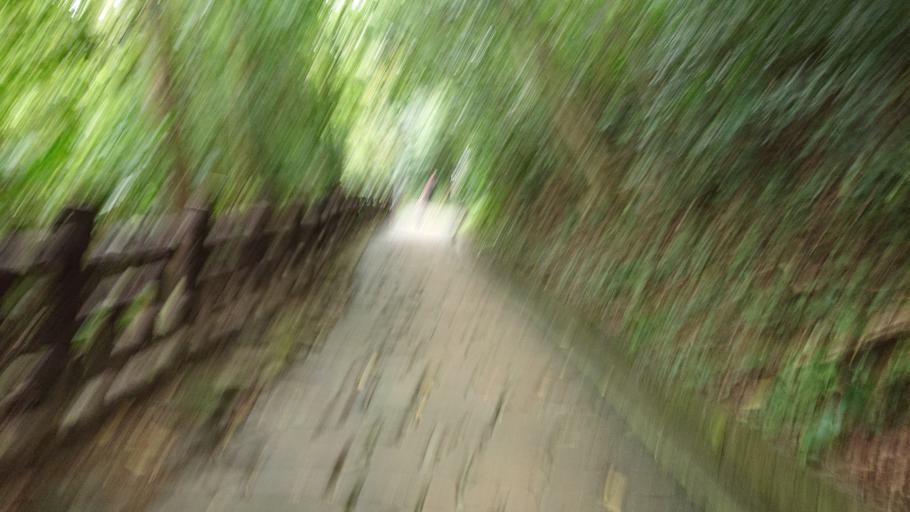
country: TW
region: Taipei
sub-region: Taipei
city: Banqiao
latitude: 24.9565
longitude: 121.4441
